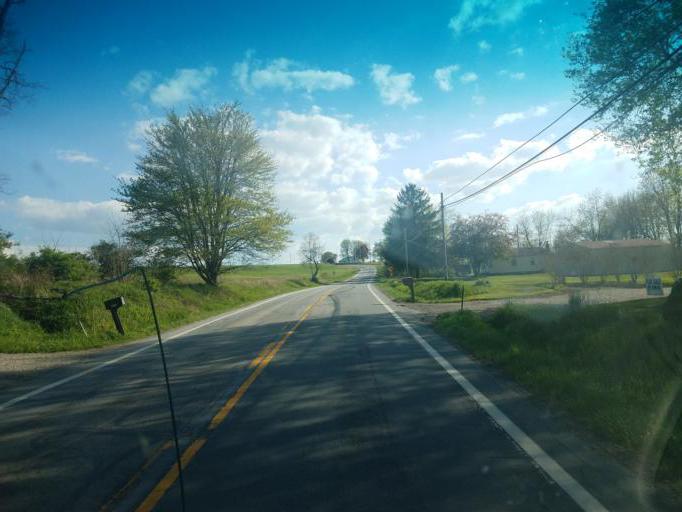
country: US
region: Ohio
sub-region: Wayne County
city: Wooster
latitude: 40.7267
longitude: -81.9422
